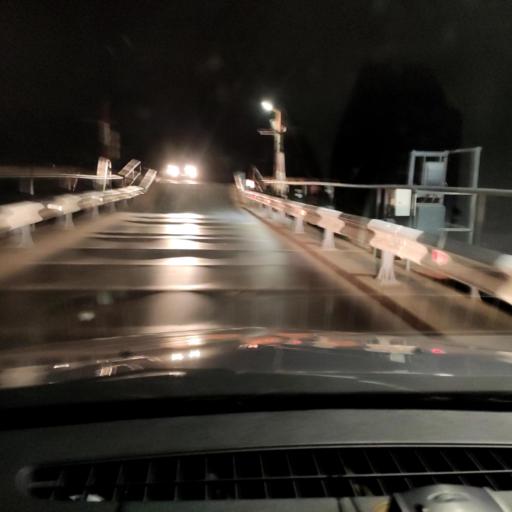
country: RU
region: Voronezj
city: Shilovo
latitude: 51.5411
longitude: 39.0790
